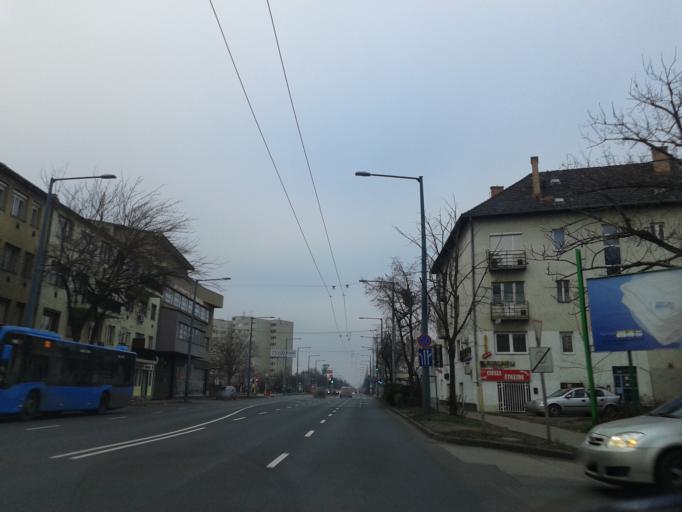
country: HU
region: Budapest
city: Budapest XIV. keruelet
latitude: 47.5024
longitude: 19.1170
